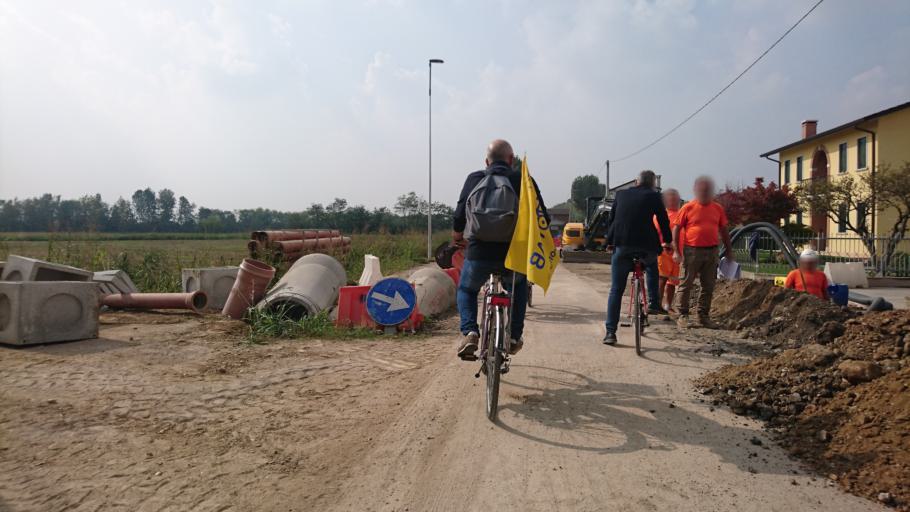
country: IT
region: Veneto
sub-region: Provincia di Vicenza
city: Grisignano di Zocco
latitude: 45.4850
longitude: 11.7211
